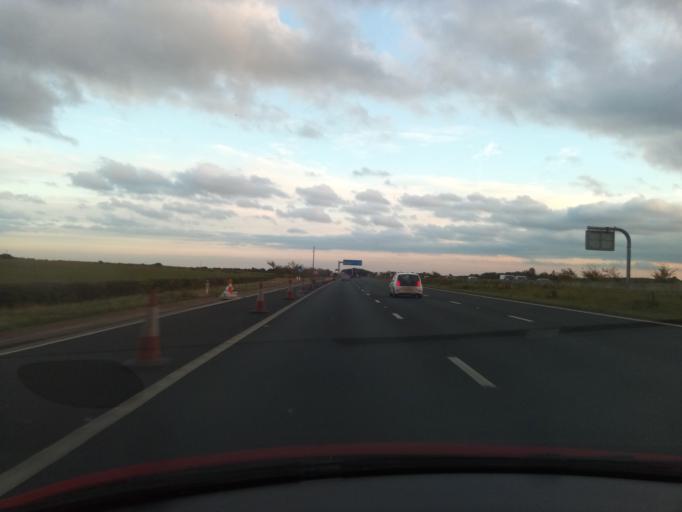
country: GB
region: England
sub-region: North Yorkshire
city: Boroughbridge
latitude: 54.1584
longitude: -1.4435
